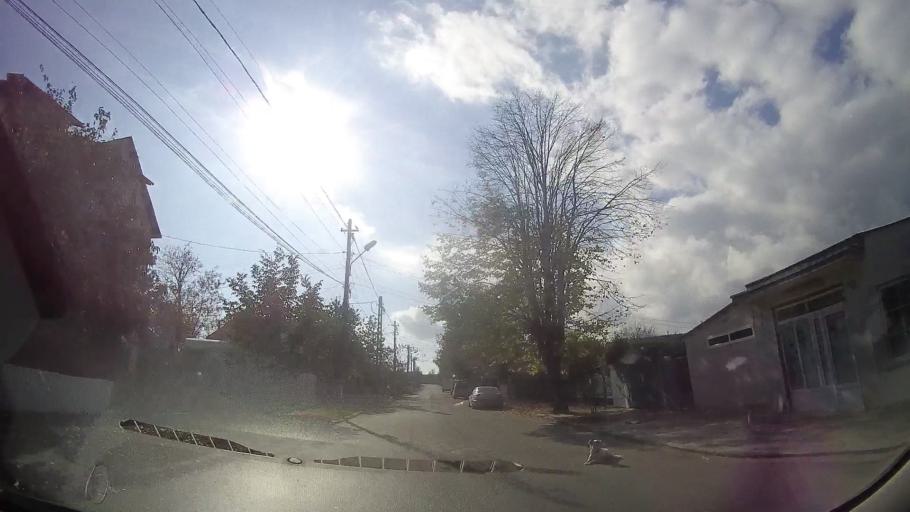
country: RO
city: Eforie Sud
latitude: 44.0197
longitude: 28.6483
